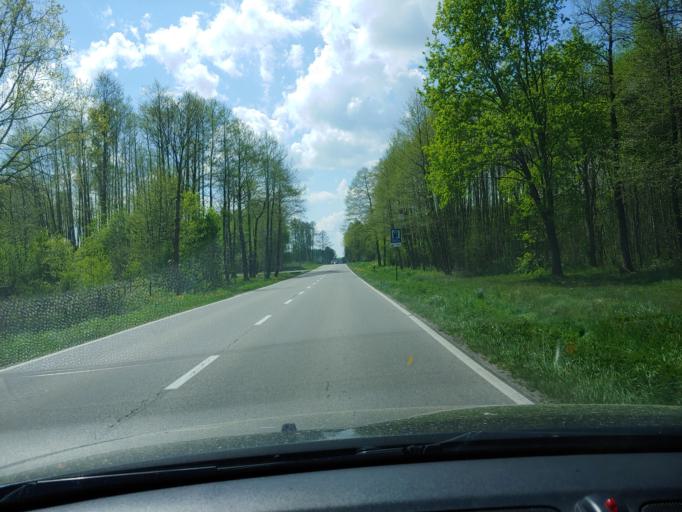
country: PL
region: Subcarpathian Voivodeship
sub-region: Powiat mielecki
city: Wadowice Gorne
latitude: 50.2510
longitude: 21.3171
